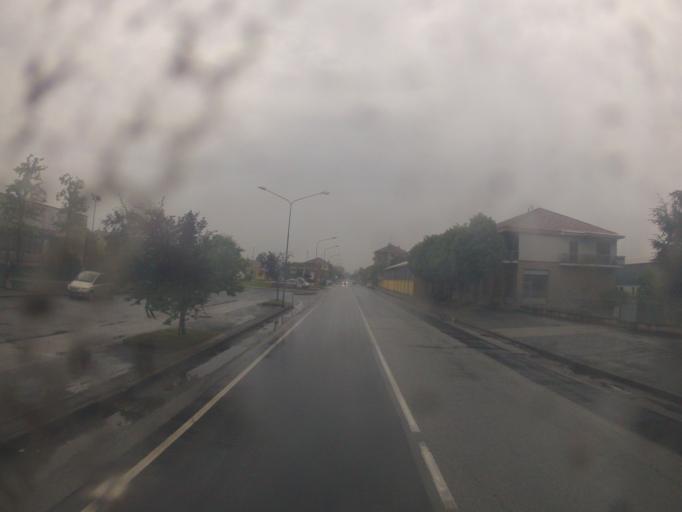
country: IT
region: Piedmont
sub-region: Provincia di Torino
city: La Loggia
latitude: 44.9476
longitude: 7.6694
